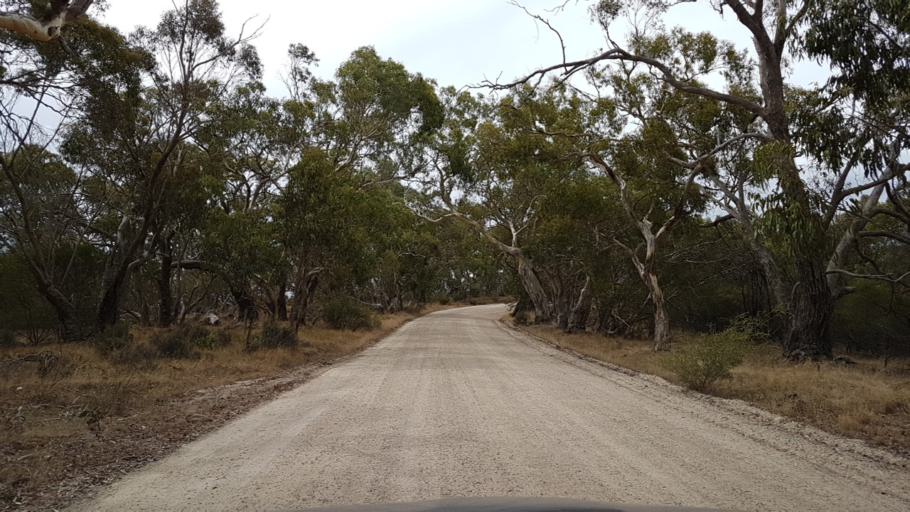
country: AU
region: South Australia
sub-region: Adelaide Hills
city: Birdwood
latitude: -34.7693
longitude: 138.9899
